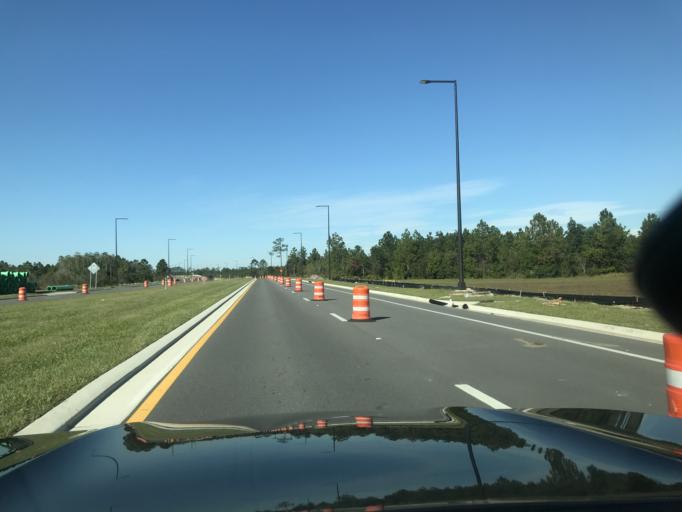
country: US
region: Florida
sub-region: Polk County
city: Citrus Ridge
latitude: 28.3795
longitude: -81.6242
